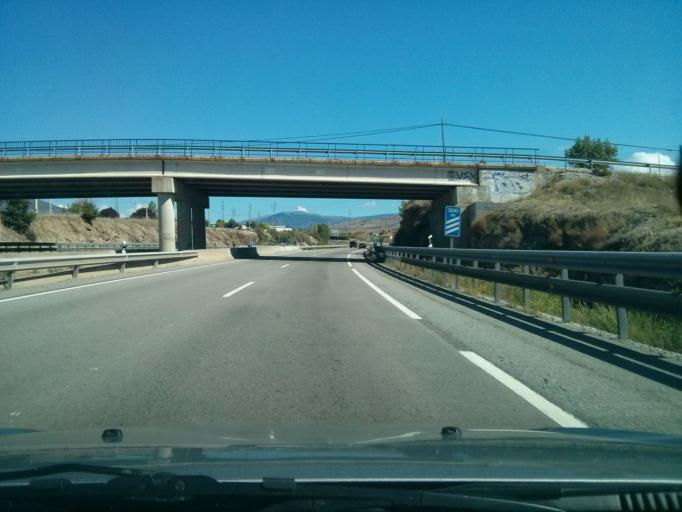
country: ES
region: Madrid
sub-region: Provincia de Madrid
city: Buitrago del Lozoya
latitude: 40.9982
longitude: -3.6407
